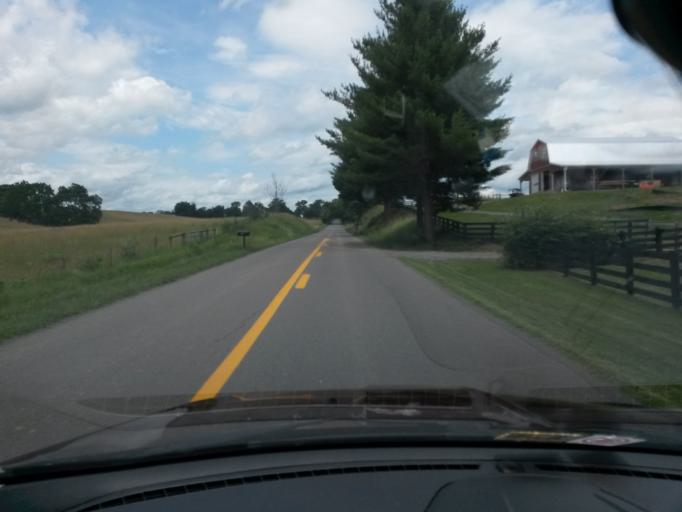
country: US
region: West Virginia
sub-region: Monroe County
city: Union
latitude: 37.5412
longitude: -80.5365
